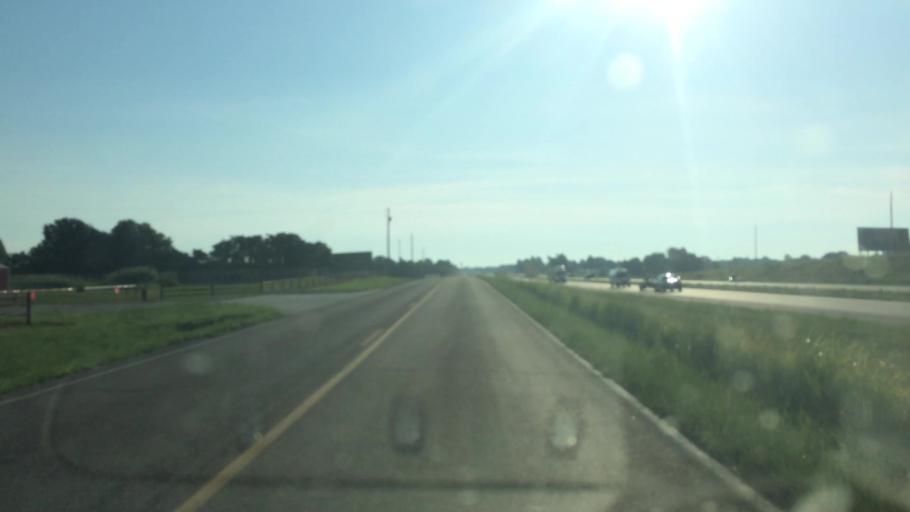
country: US
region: Missouri
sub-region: Greene County
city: Strafford
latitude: 37.2591
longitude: -93.1583
